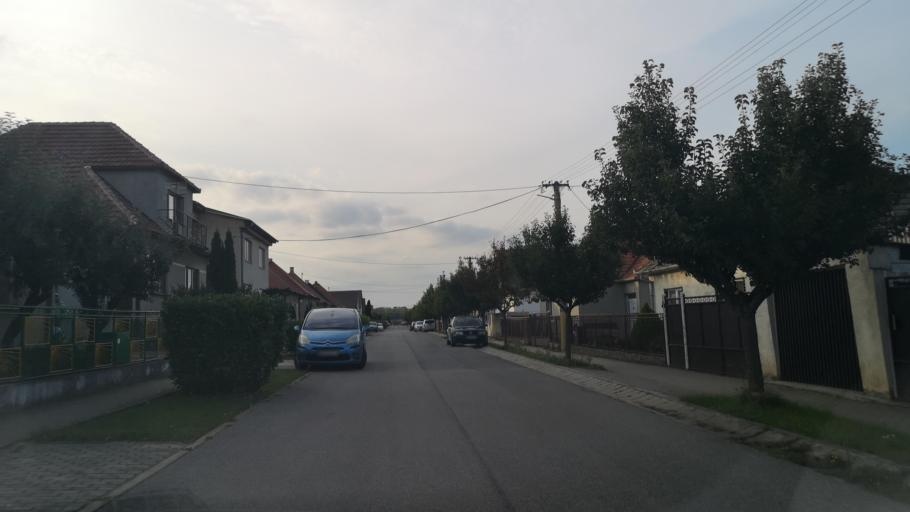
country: SK
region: Trnavsky
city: Hlohovec
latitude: 48.3669
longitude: 17.8902
